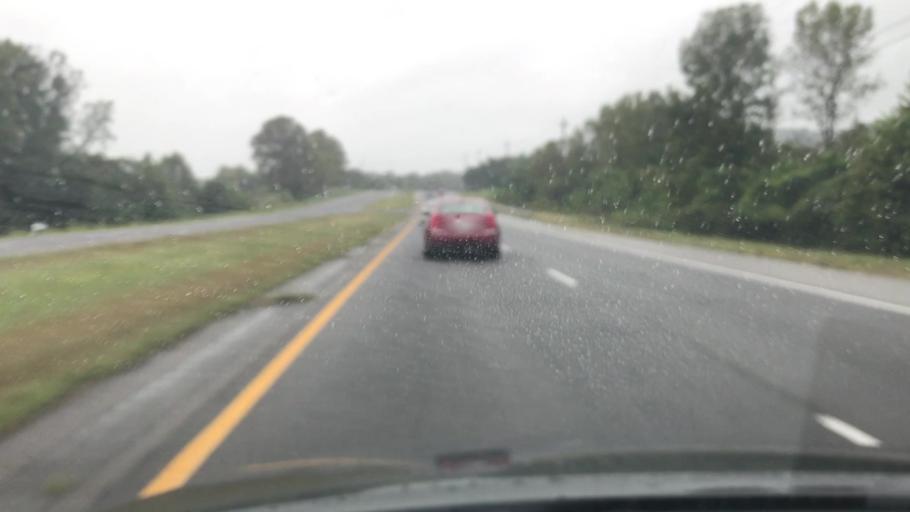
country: US
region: Tennessee
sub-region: Cheatham County
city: Ashland City
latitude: 36.2199
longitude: -86.9977
